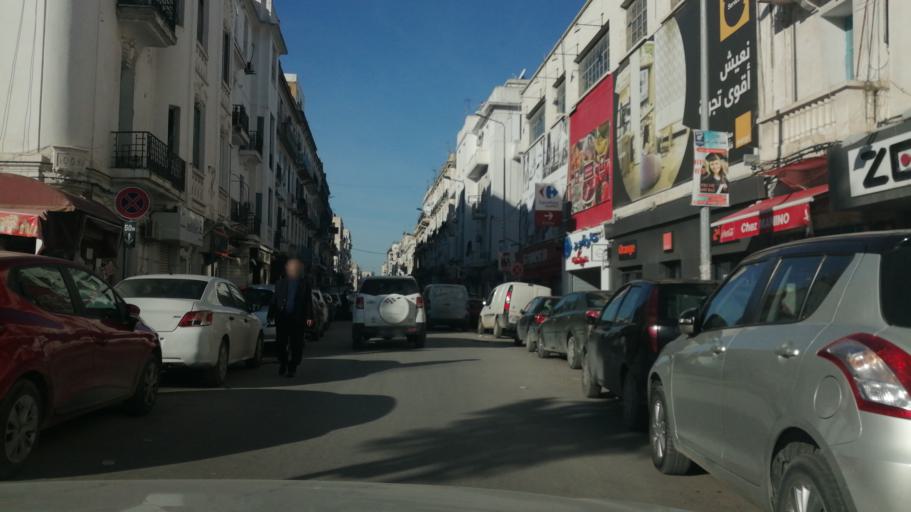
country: TN
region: Tunis
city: Tunis
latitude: 36.8061
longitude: 10.1802
